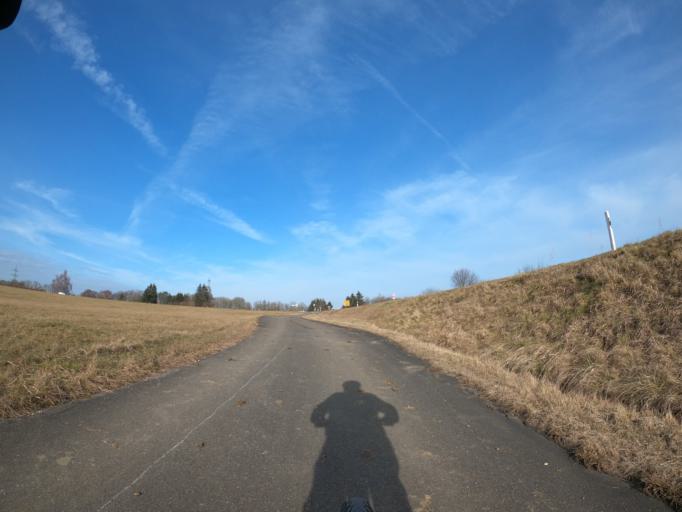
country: DE
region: Baden-Wuerttemberg
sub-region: Tuebingen Region
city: Pliezhausen
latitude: 48.5308
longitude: 9.2277
